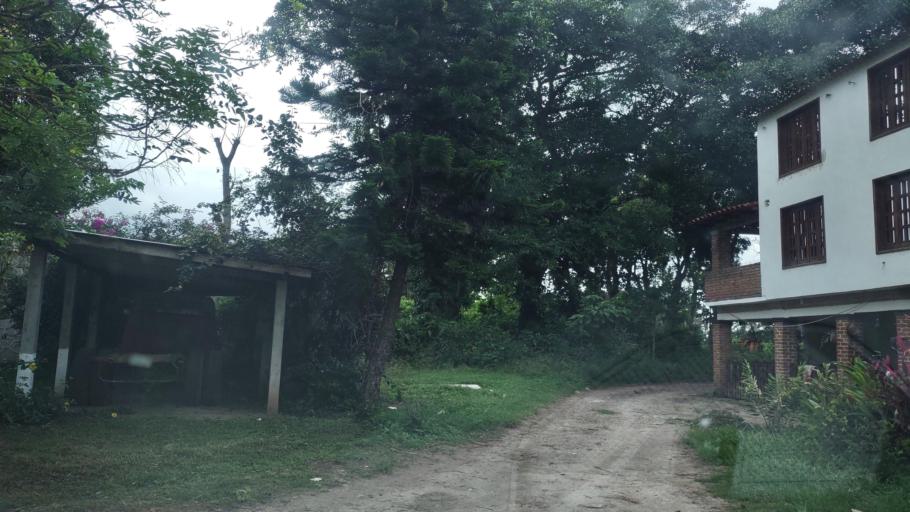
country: MX
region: Veracruz
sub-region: Coatepec
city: Bella Esperanza
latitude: 19.4463
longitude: -96.8292
